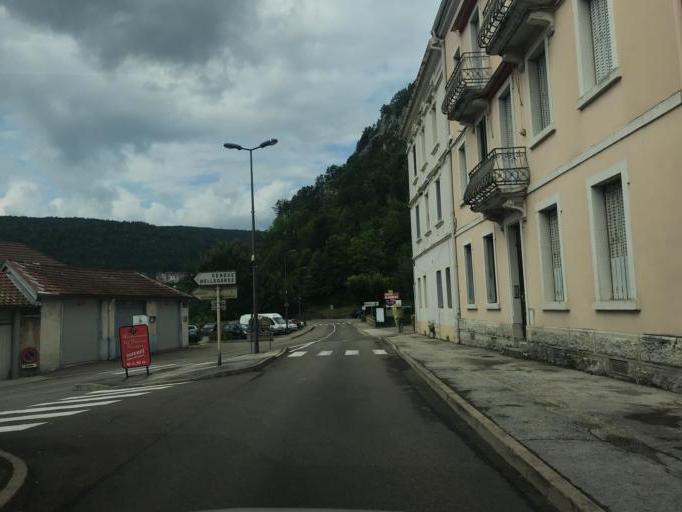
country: FR
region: Franche-Comte
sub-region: Departement du Jura
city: Saint-Claude
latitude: 46.3833
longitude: 5.8705
